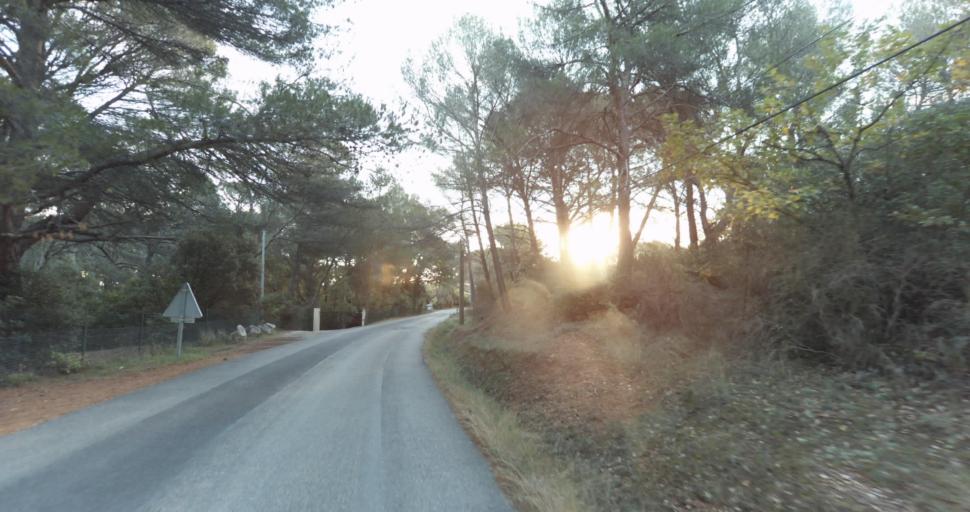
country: FR
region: Provence-Alpes-Cote d'Azur
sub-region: Departement des Bouches-du-Rhone
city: Venelles
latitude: 43.5766
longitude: 5.4865
